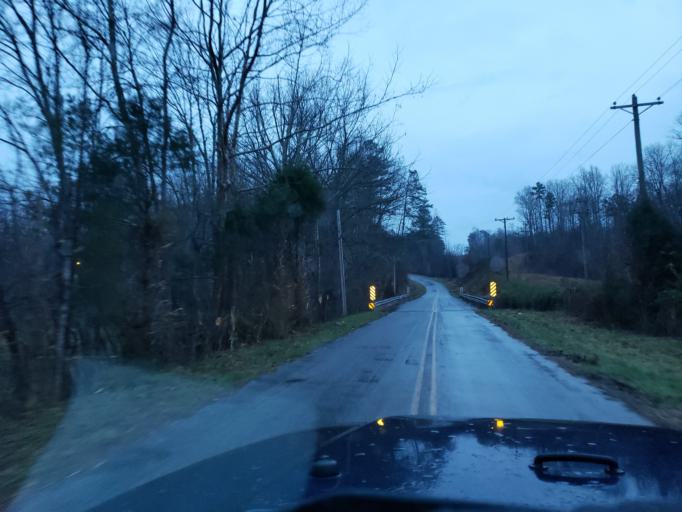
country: US
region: North Carolina
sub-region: Cleveland County
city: White Plains
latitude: 35.1460
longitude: -81.4098
